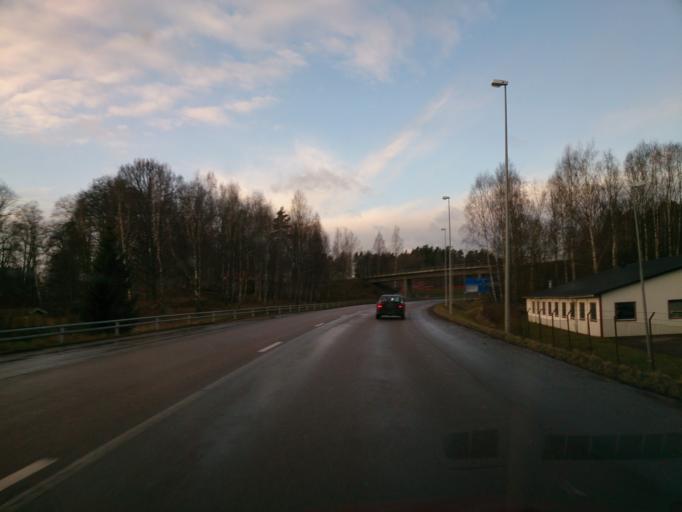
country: SE
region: OEstergoetland
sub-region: Atvidabergs Kommun
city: Atvidaberg
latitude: 58.2057
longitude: 15.9937
